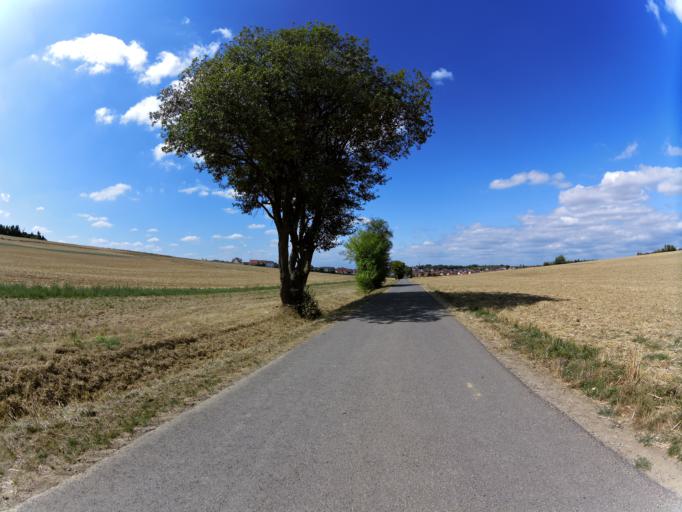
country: DE
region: Bavaria
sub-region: Regierungsbezirk Unterfranken
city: Waldbuttelbrunn
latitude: 49.8019
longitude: 9.8345
